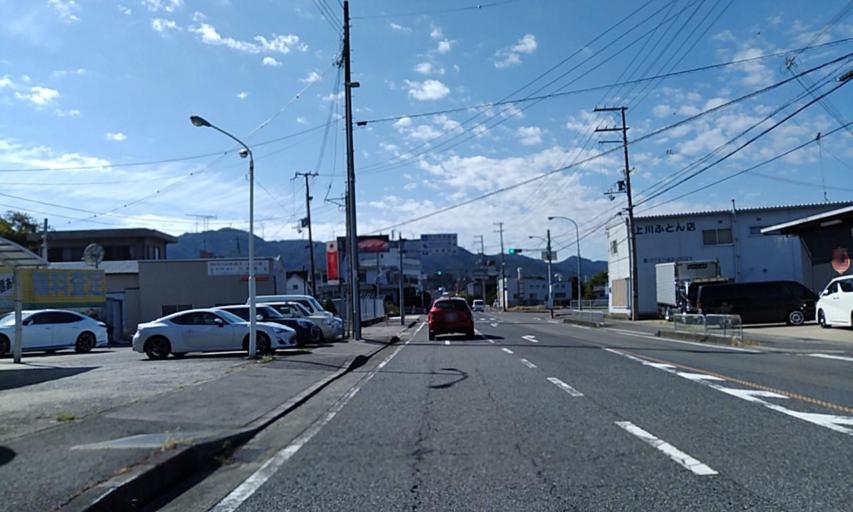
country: JP
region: Wakayama
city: Kainan
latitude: 34.0257
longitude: 135.1814
